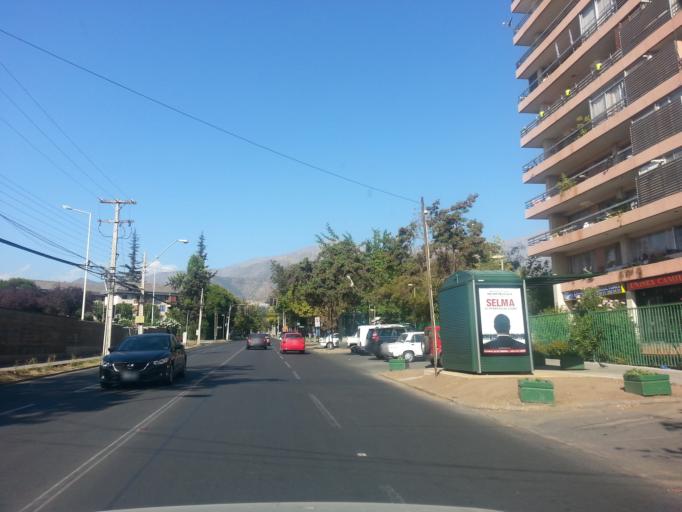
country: CL
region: Santiago Metropolitan
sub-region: Provincia de Santiago
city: Villa Presidente Frei, Nunoa, Santiago, Chile
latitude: -33.4255
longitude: -70.5536
